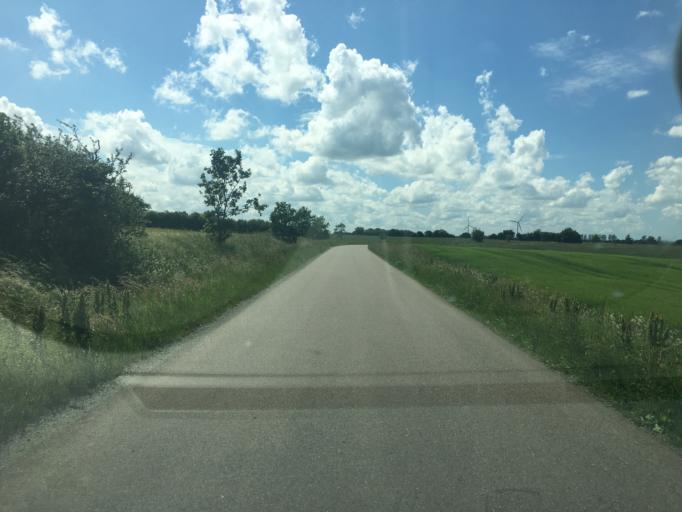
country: DK
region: South Denmark
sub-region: Haderslev Kommune
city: Vojens
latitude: 55.2738
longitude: 9.3432
